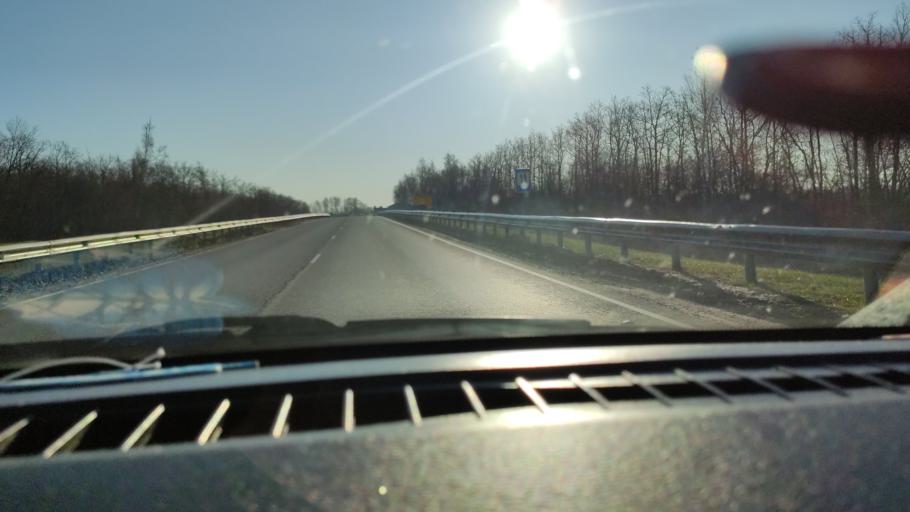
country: RU
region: Saratov
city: Balakovo
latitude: 52.0958
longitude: 47.7222
